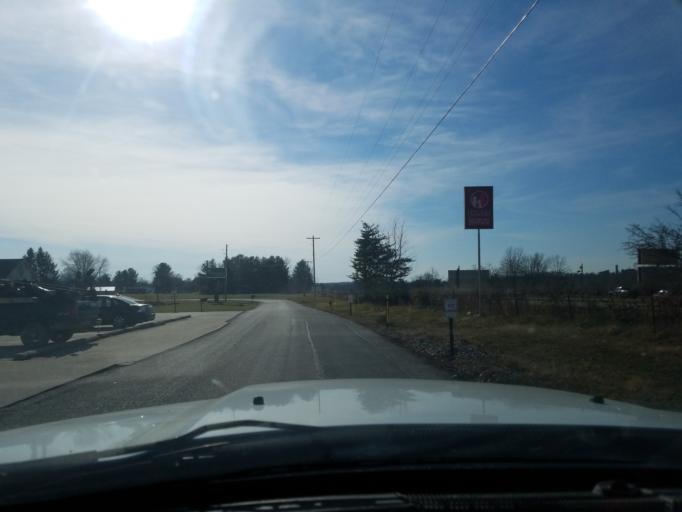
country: US
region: Ohio
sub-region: Athens County
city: Athens
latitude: 39.2349
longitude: -82.1944
